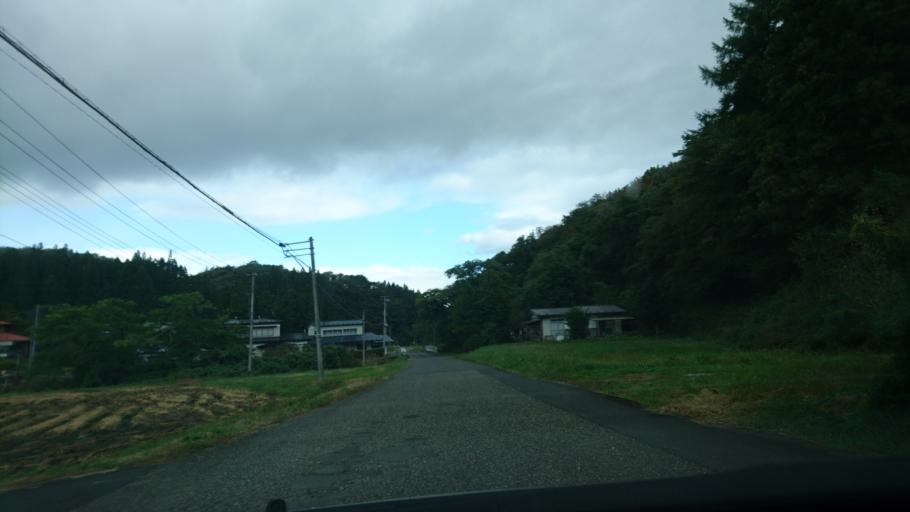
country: JP
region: Iwate
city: Ichinoseki
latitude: 38.9026
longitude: 141.0824
